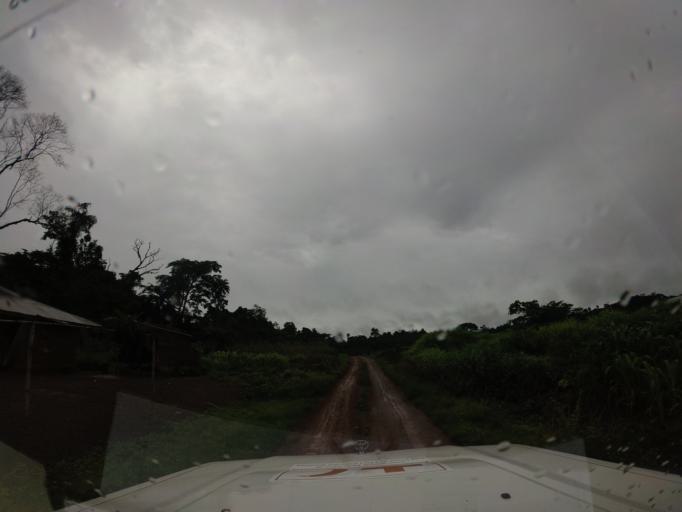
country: SL
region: Eastern Province
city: Kenema
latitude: 7.7145
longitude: -11.1873
